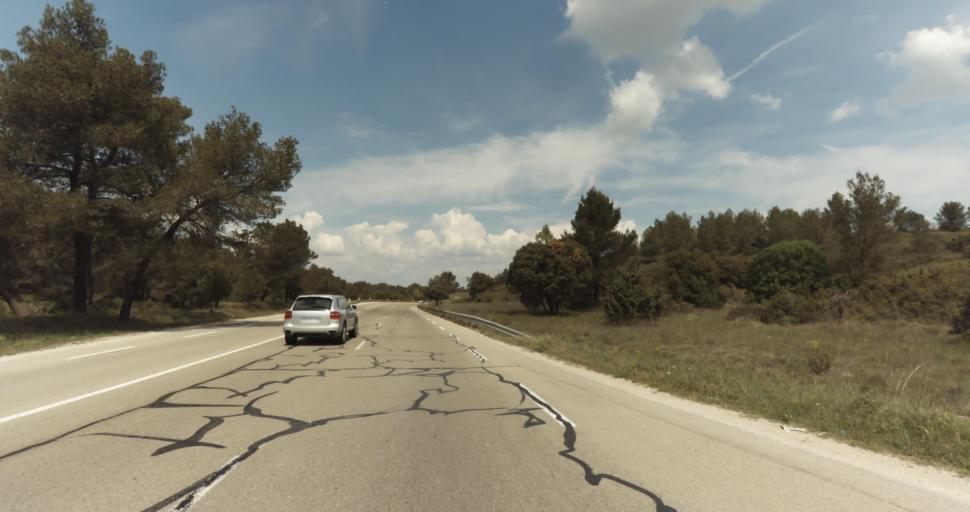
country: FR
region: Languedoc-Roussillon
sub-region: Departement du Gard
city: La Calmette
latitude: 43.8949
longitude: 4.2895
